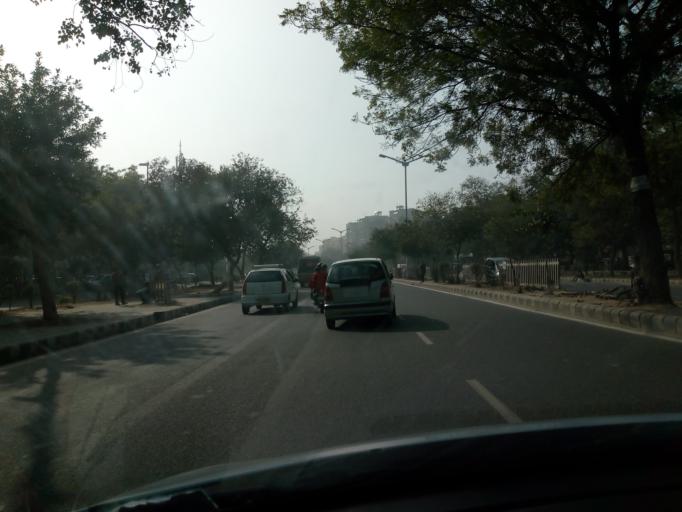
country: IN
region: NCT
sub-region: West Delhi
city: Nangloi Jat
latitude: 28.6048
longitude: 77.0469
